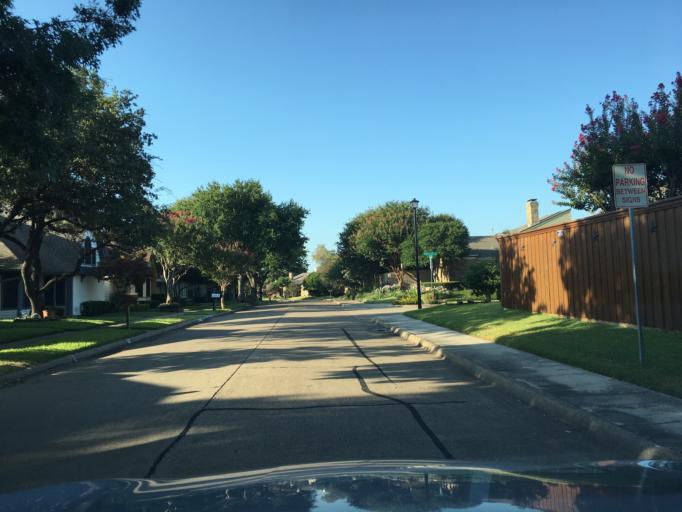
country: US
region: Texas
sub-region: Dallas County
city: Addison
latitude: 32.9687
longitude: -96.8559
